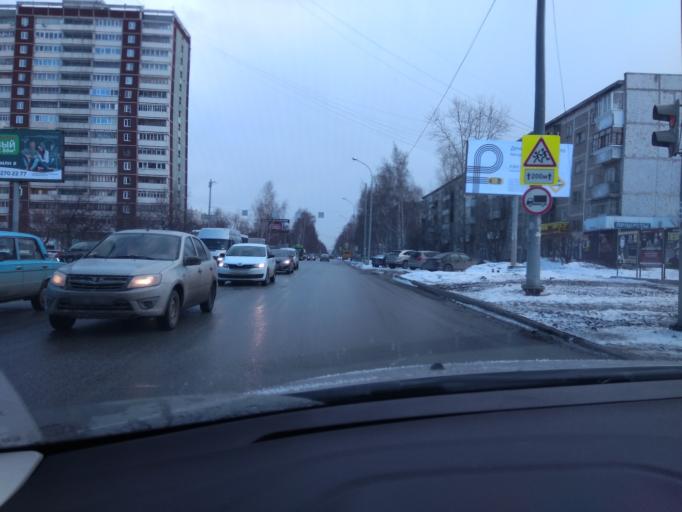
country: RU
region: Sverdlovsk
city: Sovkhoznyy
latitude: 56.8100
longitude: 60.5465
